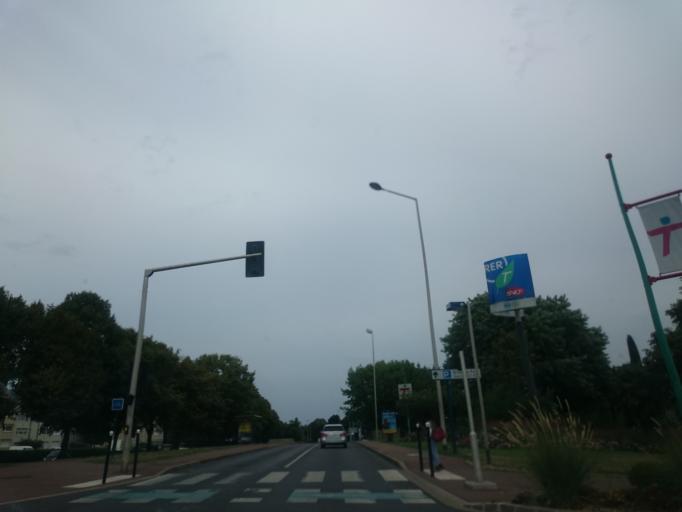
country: FR
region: Ile-de-France
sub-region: Departement de l'Essonne
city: Evry
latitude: 48.6236
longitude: 2.4500
